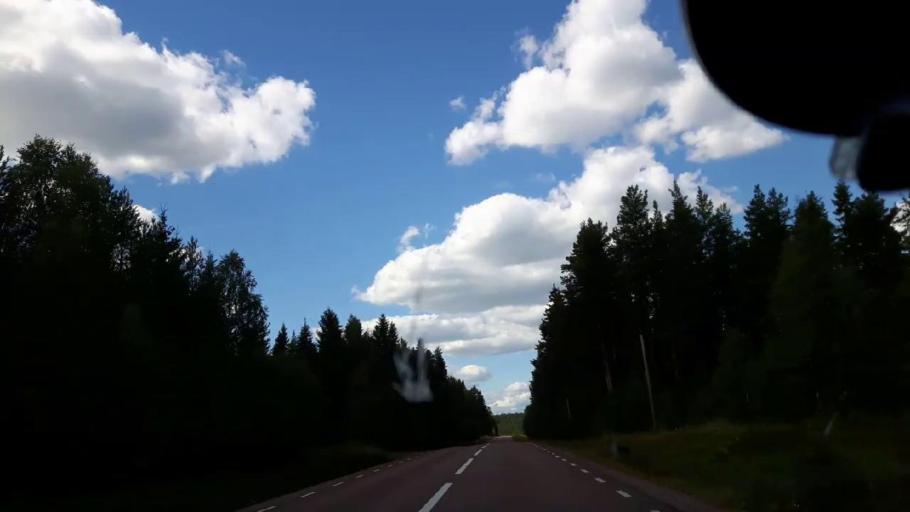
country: SE
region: Jaemtland
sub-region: Ragunda Kommun
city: Hammarstrand
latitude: 63.0188
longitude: 16.5611
